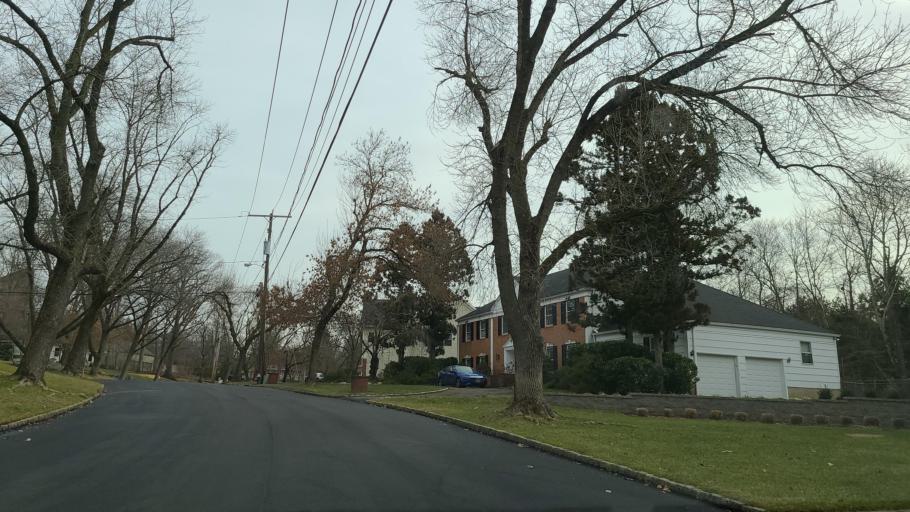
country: US
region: New Jersey
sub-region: Essex County
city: Short Hills
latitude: 40.7562
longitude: -74.3169
